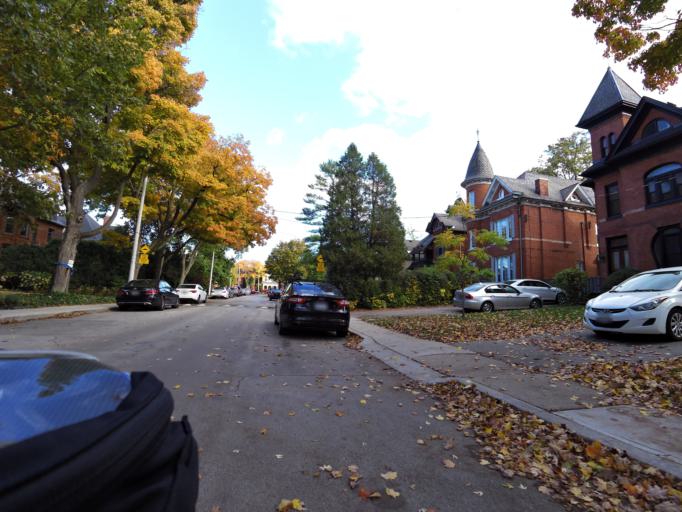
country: CA
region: Ontario
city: Hamilton
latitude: 43.2500
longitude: -79.8841
